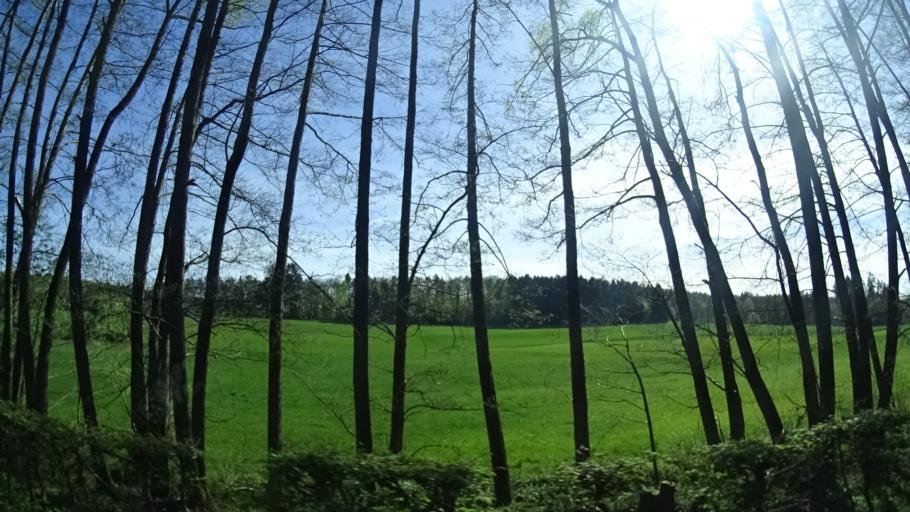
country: DE
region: Bavaria
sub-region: Regierungsbezirk Unterfranken
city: Burgpreppach
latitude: 50.1032
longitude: 10.6486
